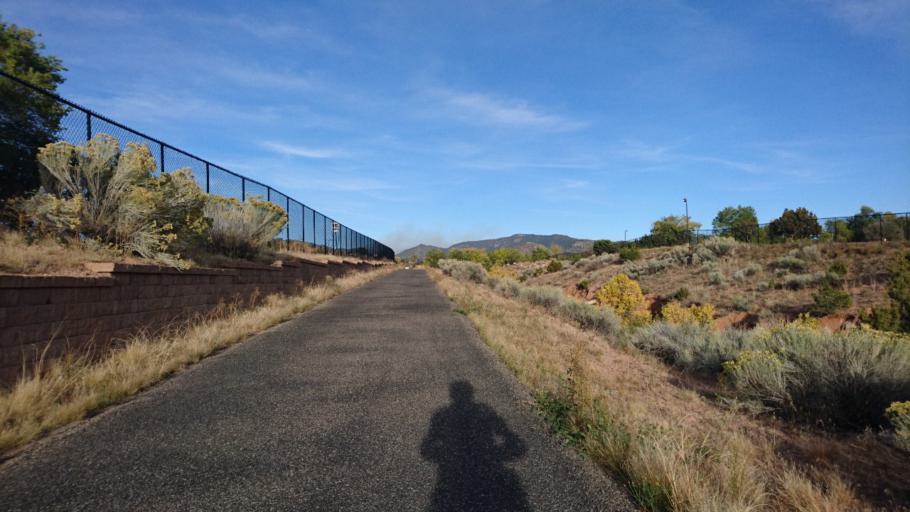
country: US
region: New Mexico
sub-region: Santa Fe County
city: Santa Fe
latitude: 35.6480
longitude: -105.9676
